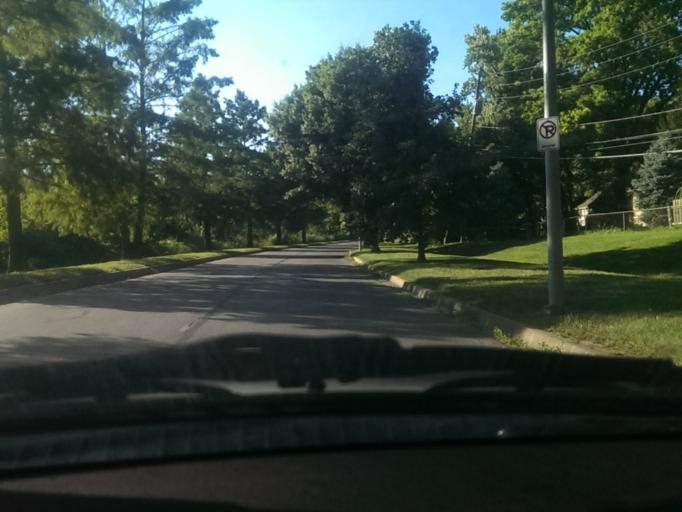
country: US
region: Kansas
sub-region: Johnson County
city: Leawood
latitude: 38.9640
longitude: -94.6042
